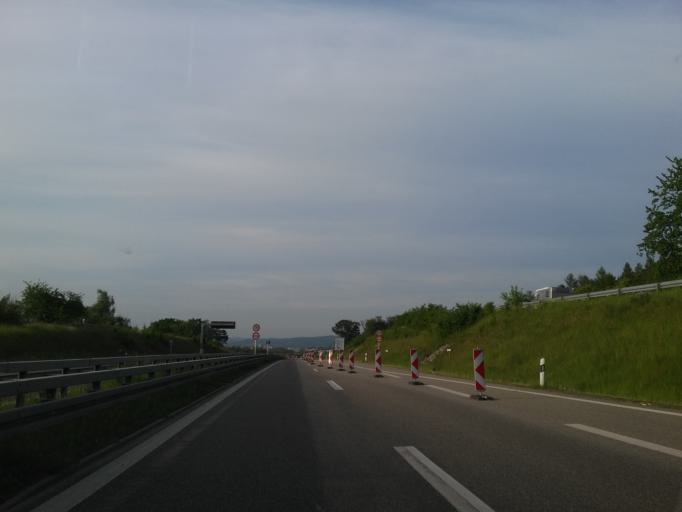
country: DE
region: Baden-Wuerttemberg
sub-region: Regierungsbezirk Stuttgart
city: Leutenbach
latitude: 48.9035
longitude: 9.4216
